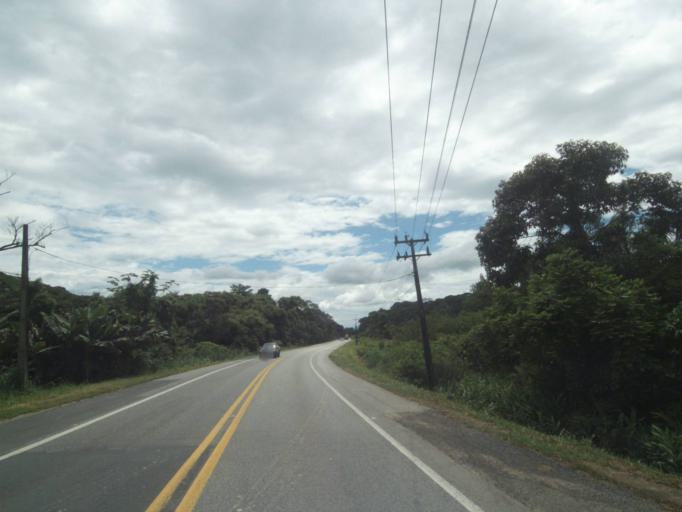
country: BR
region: Parana
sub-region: Antonina
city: Antonina
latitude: -25.4475
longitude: -48.7716
